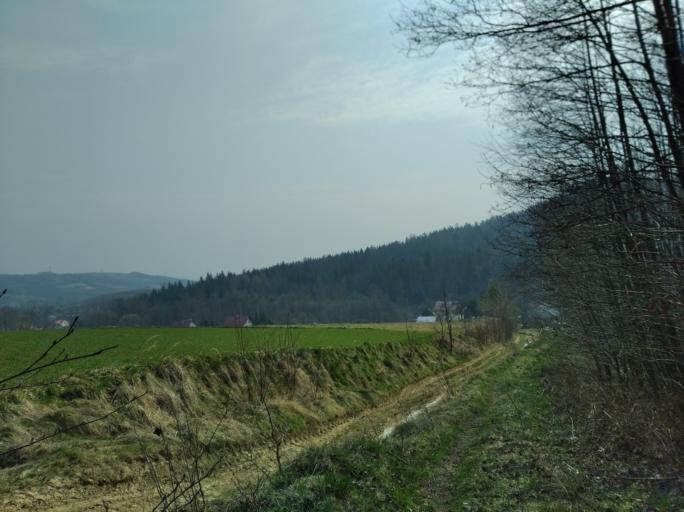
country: PL
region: Subcarpathian Voivodeship
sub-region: Powiat strzyzowski
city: Strzyzow
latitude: 49.8144
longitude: 21.8264
